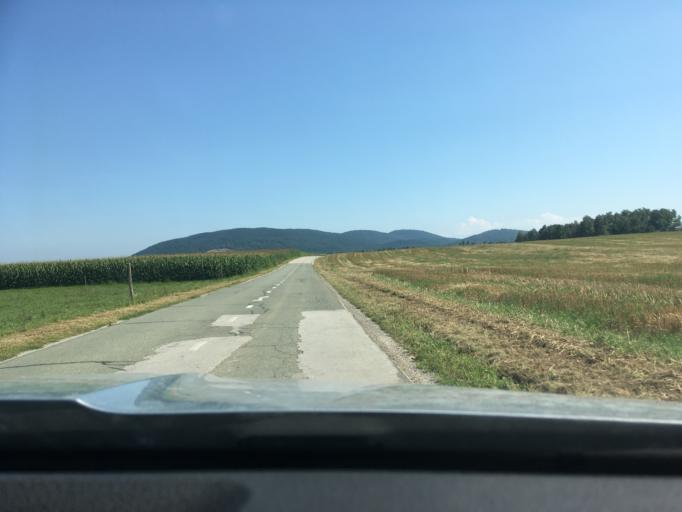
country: SI
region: Metlika
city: Metlika
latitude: 45.5853
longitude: 15.2825
